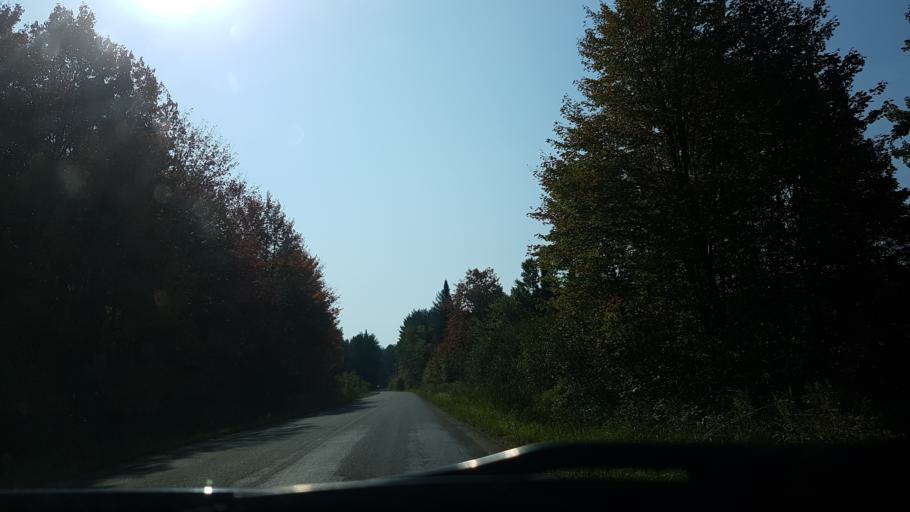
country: CA
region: Ontario
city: Bracebridge
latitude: 44.9694
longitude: -79.2562
